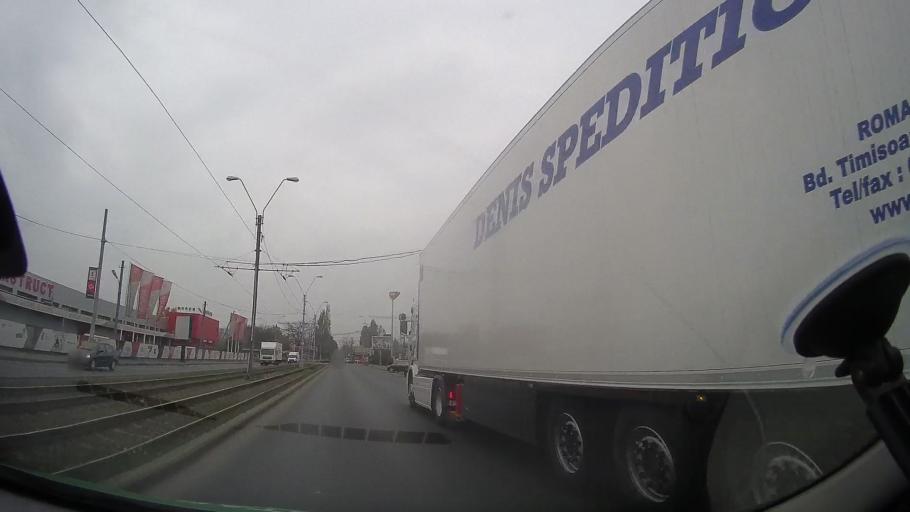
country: RO
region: Ilfov
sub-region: Comuna Chiajna
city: Rosu
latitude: 44.4240
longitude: 25.9994
